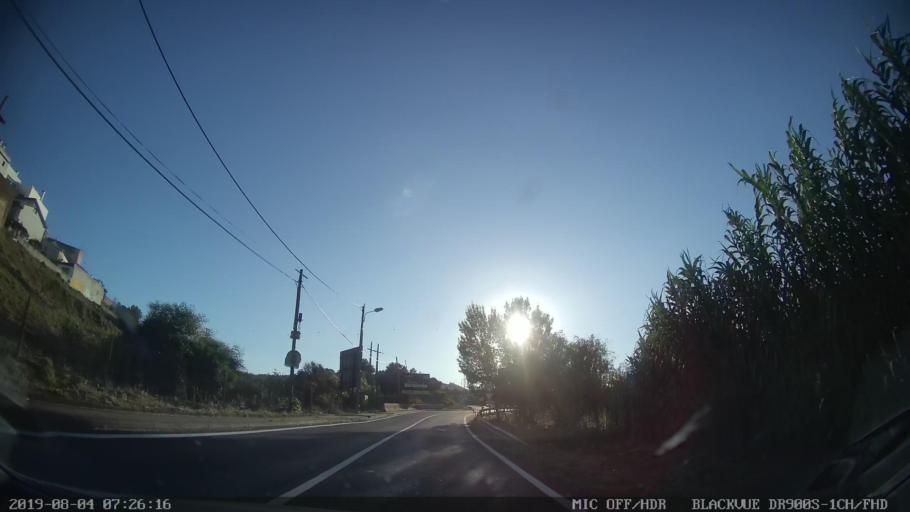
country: PT
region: Lisbon
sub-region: Loures
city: Santa Iria da Azoia
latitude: 38.8476
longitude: -9.0868
